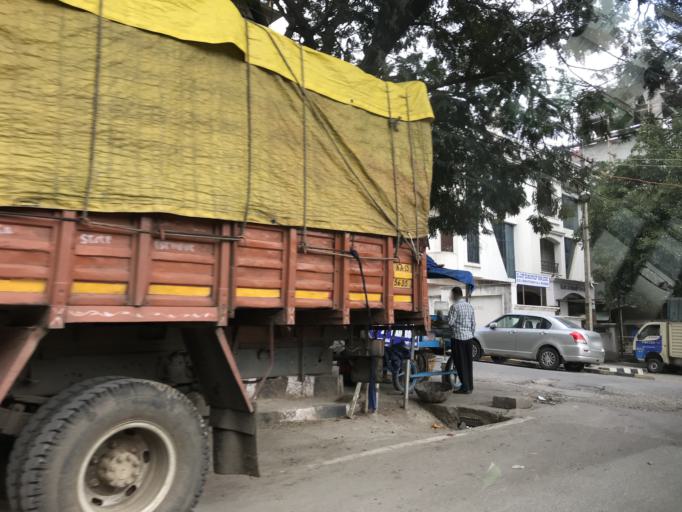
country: IN
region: Karnataka
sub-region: Bangalore Urban
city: Bangalore
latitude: 12.9579
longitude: 77.5644
